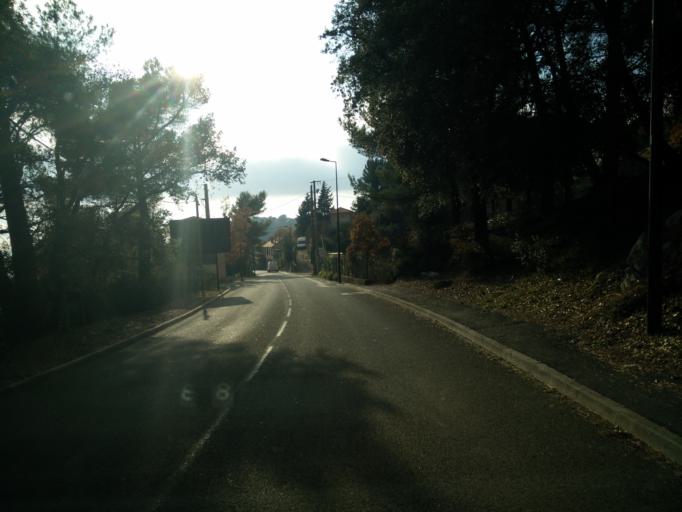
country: FR
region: Provence-Alpes-Cote d'Azur
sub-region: Departement des Alpes-Maritimes
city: Grasse
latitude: 43.6664
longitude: 6.9226
